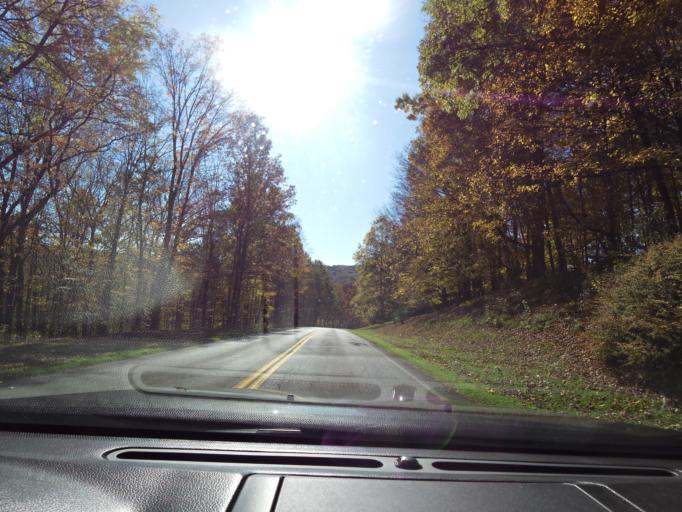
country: US
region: New York
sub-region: Wyoming County
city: Castile
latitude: 42.5930
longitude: -78.0132
